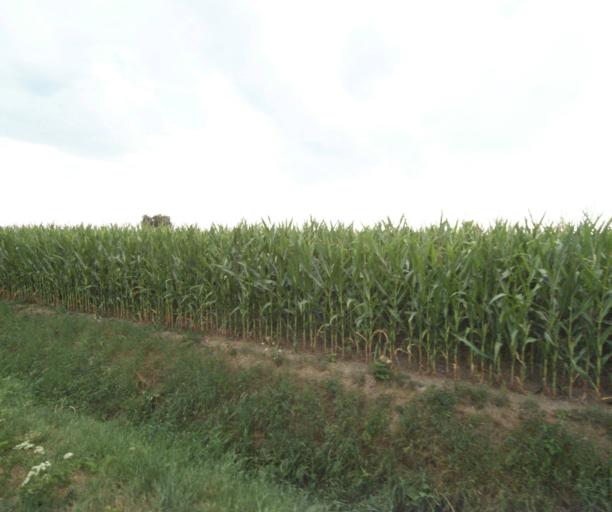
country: FR
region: Nord-Pas-de-Calais
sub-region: Departement du Nord
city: Deulemont
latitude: 50.7299
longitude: 2.9555
